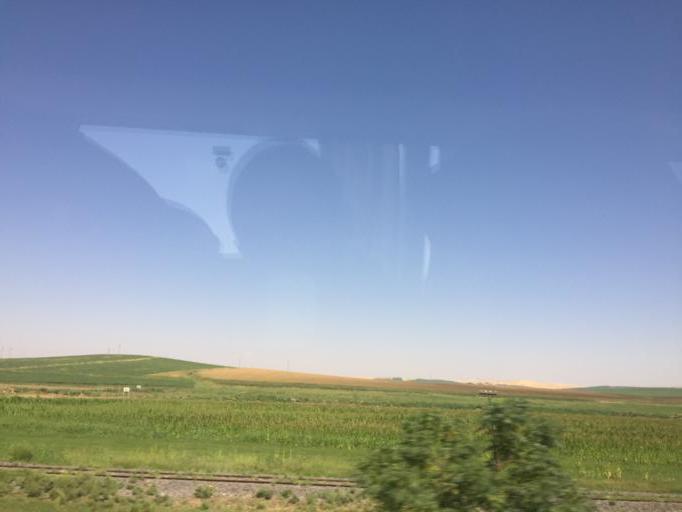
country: TR
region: Diyarbakir
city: Aralik
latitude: 37.8499
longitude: 40.7348
